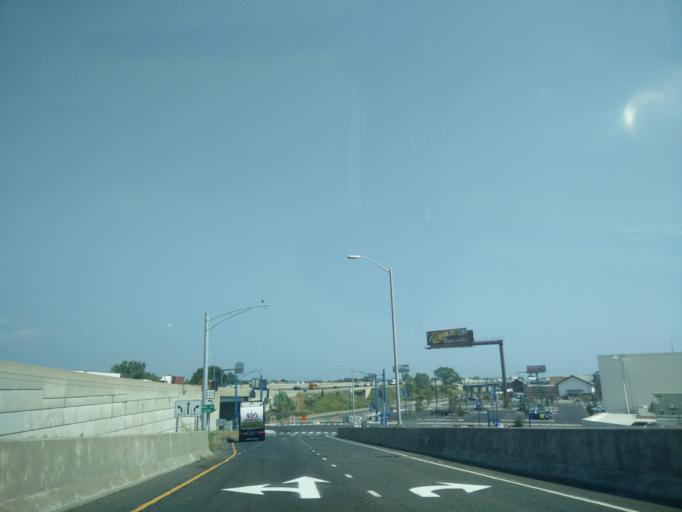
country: US
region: Connecticut
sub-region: Fairfield County
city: Bridgeport
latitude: 41.1786
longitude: -73.1824
